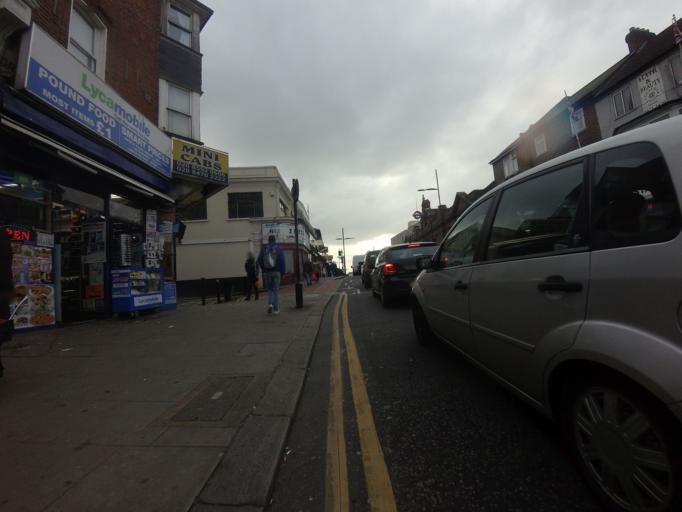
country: GB
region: England
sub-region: Greater London
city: East Ham
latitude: 51.5356
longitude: 0.0354
